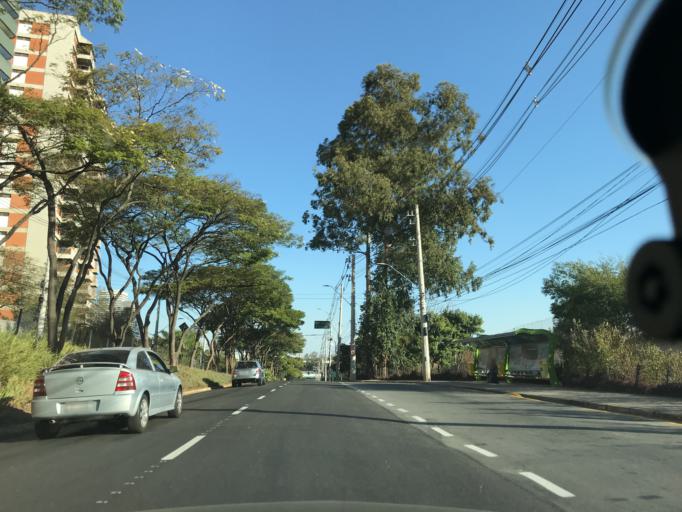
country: BR
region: Sao Paulo
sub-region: Barueri
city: Barueri
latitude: -23.4941
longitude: -46.8535
